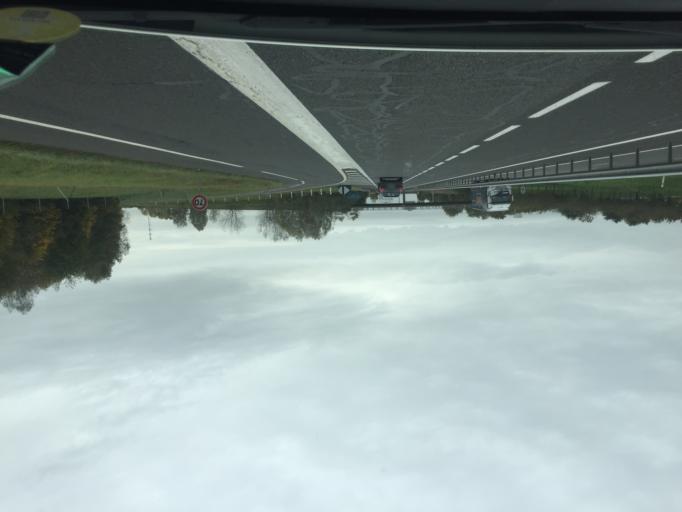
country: FR
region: Bourgogne
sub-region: Departement de l'Yonne
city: Egriselles-le-Bocage
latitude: 48.1466
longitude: 3.1636
